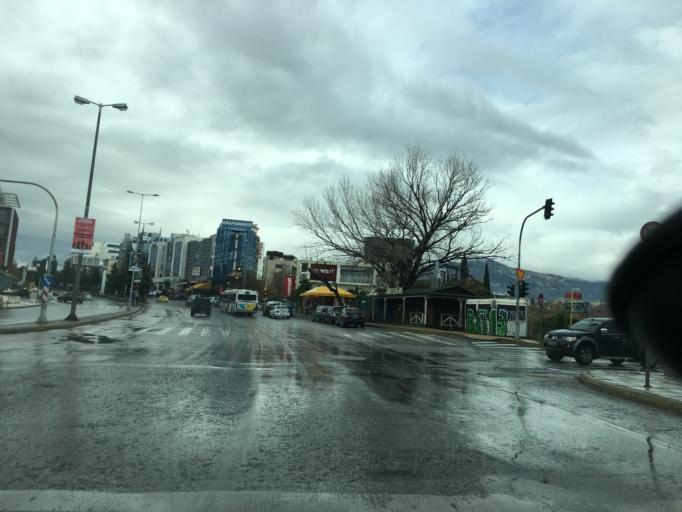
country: GR
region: Attica
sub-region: Nomarchia Athinas
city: Marousi
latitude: 38.0455
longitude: 23.8069
